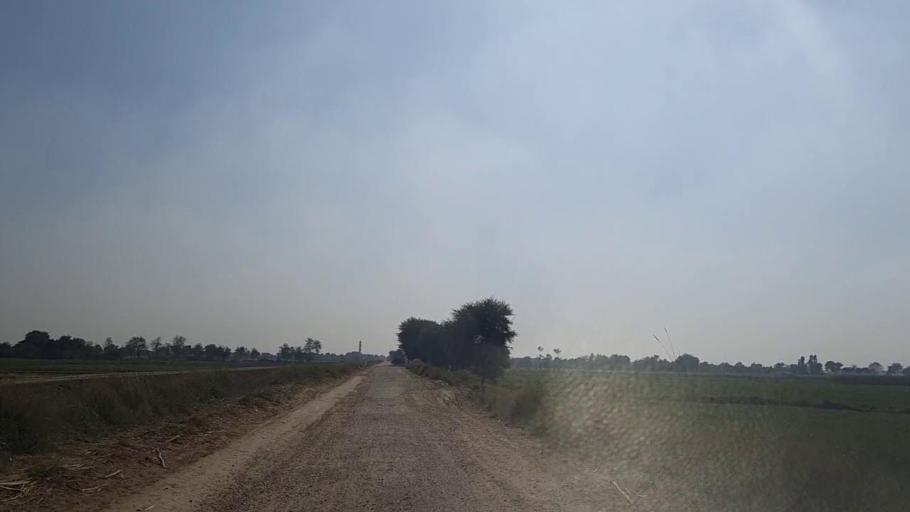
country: PK
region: Sindh
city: Shahpur Chakar
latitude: 26.1967
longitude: 68.5835
